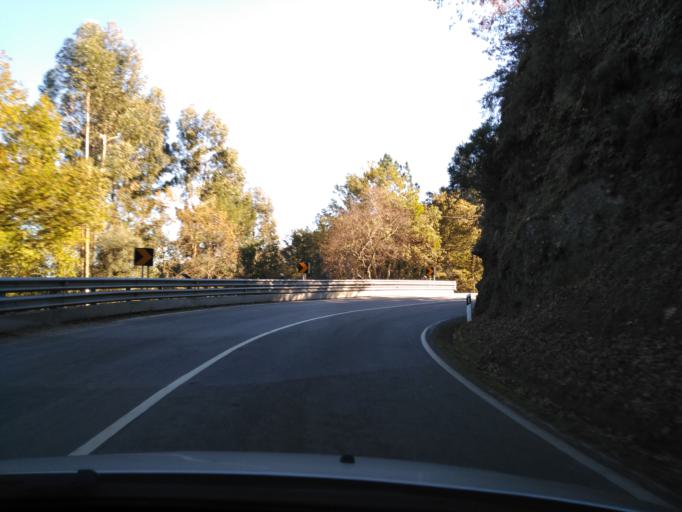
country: PT
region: Braga
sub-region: Vieira do Minho
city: Vieira do Minho
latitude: 41.6803
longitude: -8.1076
